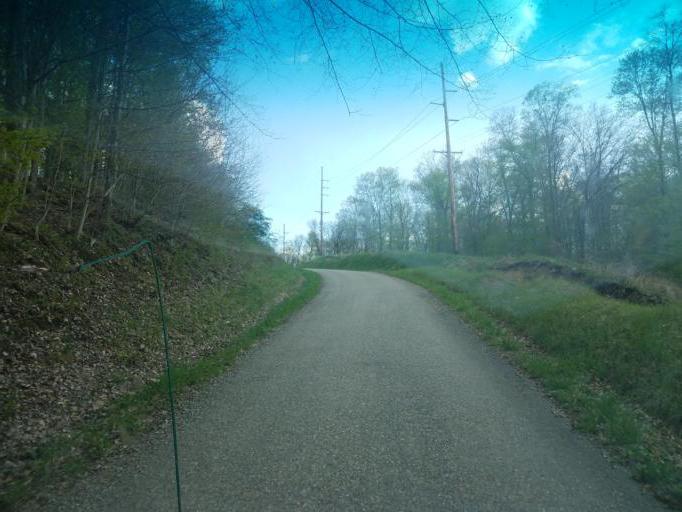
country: US
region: Ohio
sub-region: Wayne County
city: Shreve
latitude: 40.6447
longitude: -82.0333
